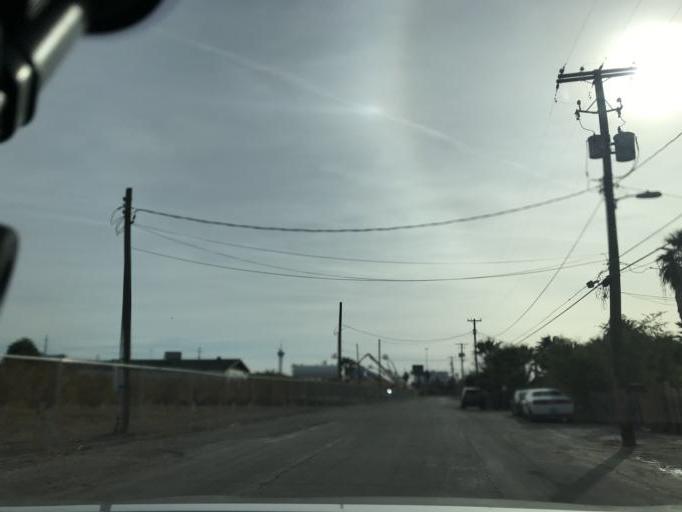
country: US
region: Nevada
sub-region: Clark County
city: Las Vegas
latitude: 36.1795
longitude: -115.1671
